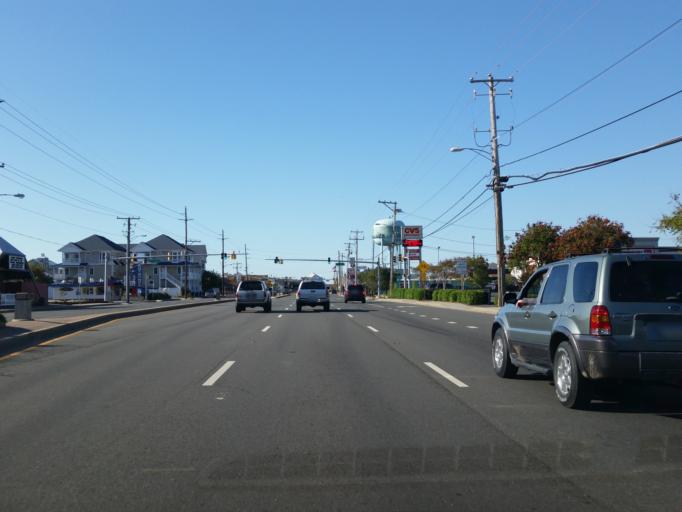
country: US
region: Maryland
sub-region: Worcester County
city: Ocean City
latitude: 38.3480
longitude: -75.0790
